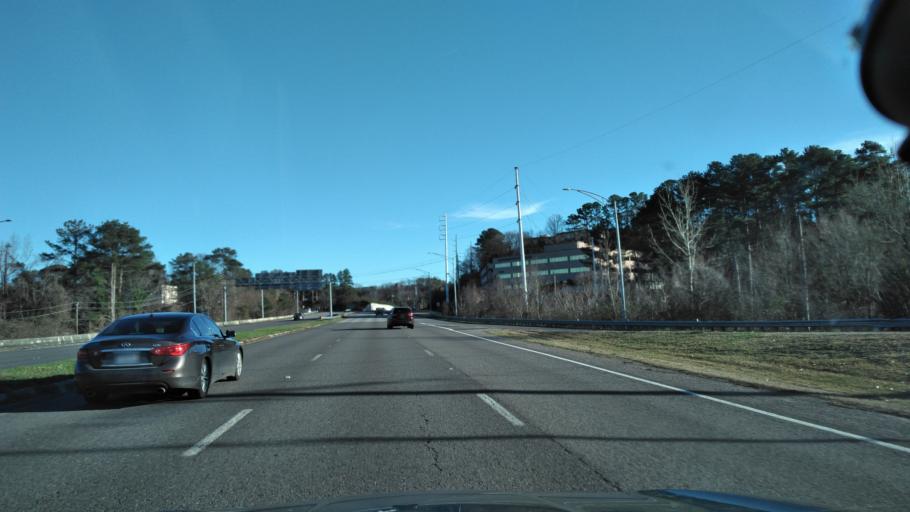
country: US
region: Alabama
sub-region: Jefferson County
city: Homewood
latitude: 33.4817
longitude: -86.7773
